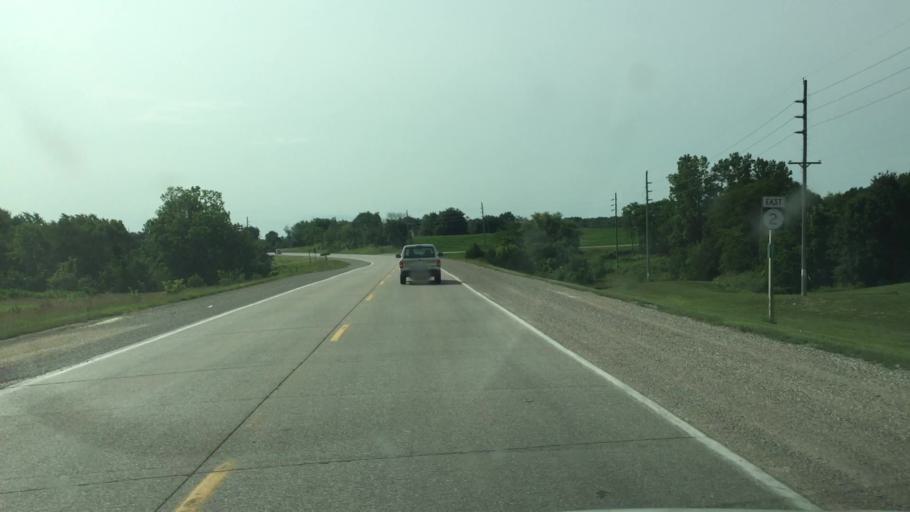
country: US
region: Illinois
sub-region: Hancock County
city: Nauvoo
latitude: 40.6350
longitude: -91.5171
